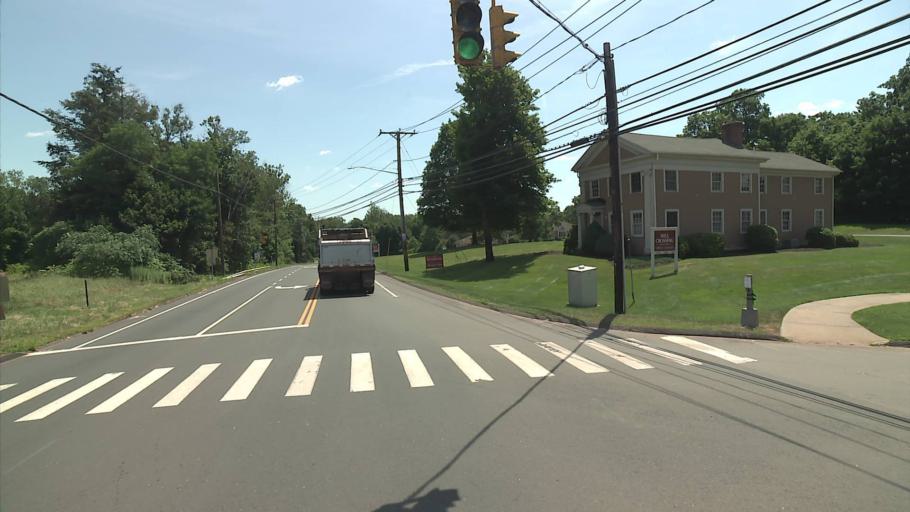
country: US
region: Connecticut
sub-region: Hartford County
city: Kensington
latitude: 41.6089
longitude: -72.7185
